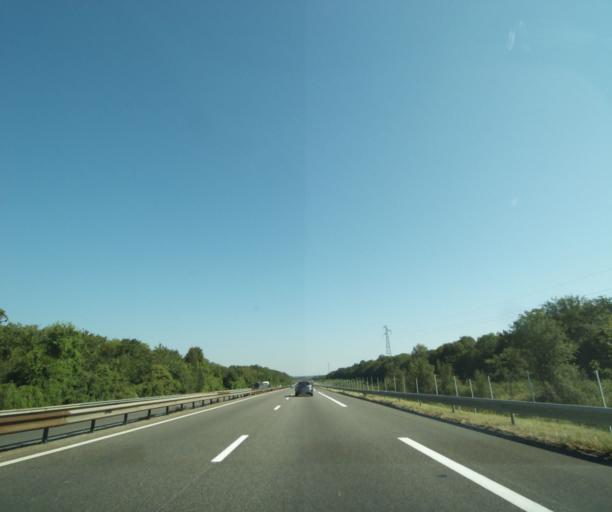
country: FR
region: Lorraine
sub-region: Departement de Meurthe-et-Moselle
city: Villers-les-Nancy
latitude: 48.6684
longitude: 6.1230
